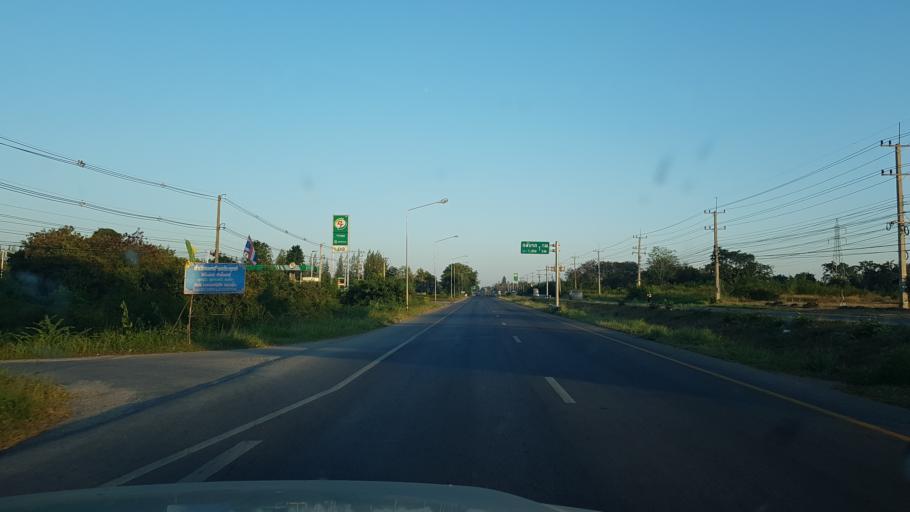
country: TH
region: Khon Kaen
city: Chum Phae
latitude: 16.5810
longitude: 102.0180
